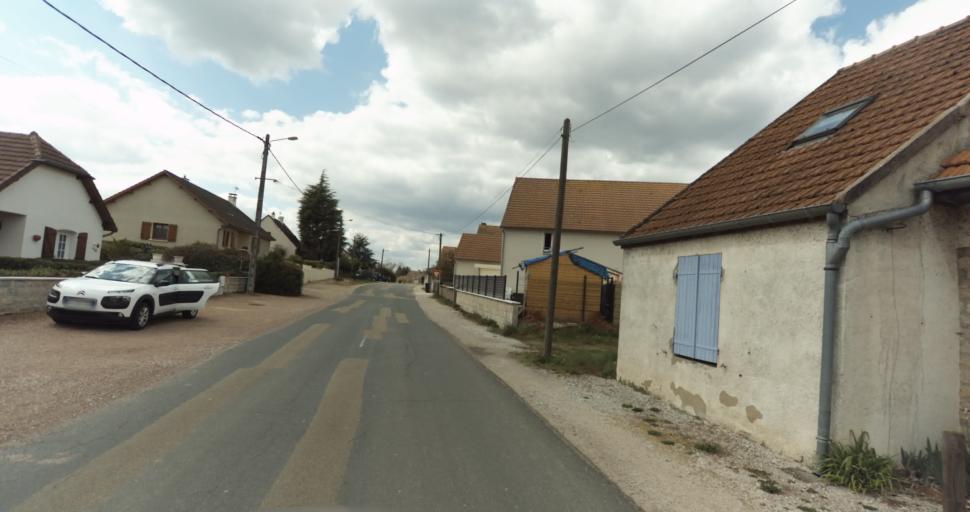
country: FR
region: Bourgogne
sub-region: Departement de la Cote-d'Or
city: Auxonne
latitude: 47.1891
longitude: 5.3991
